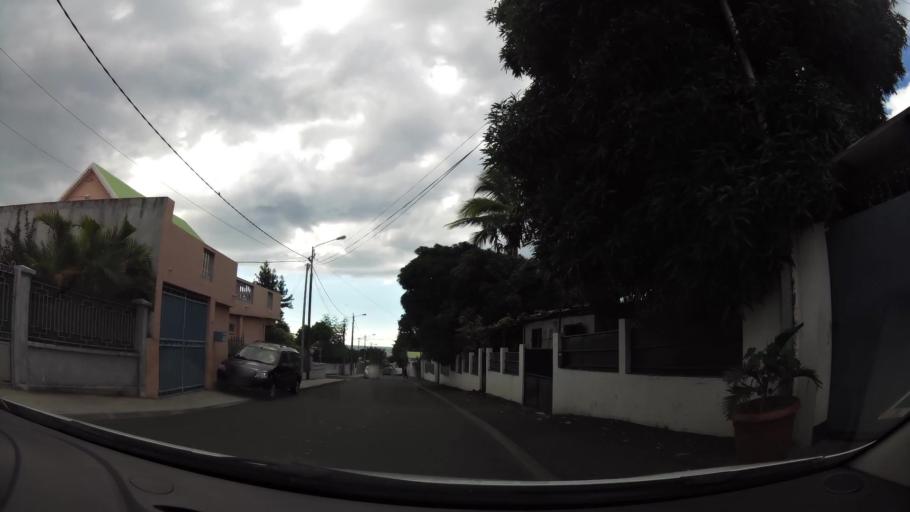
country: RE
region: Reunion
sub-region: Reunion
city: Saint-Denis
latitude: -20.8917
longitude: 55.4744
